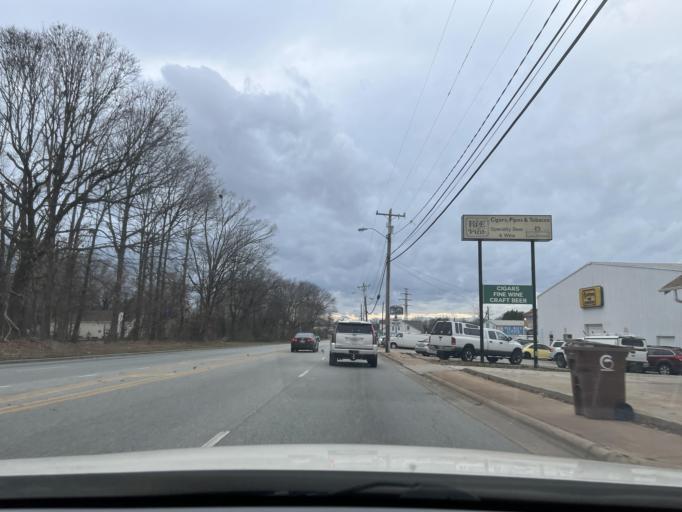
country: US
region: North Carolina
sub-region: Guilford County
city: Greensboro
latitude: 36.0611
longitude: -79.8560
